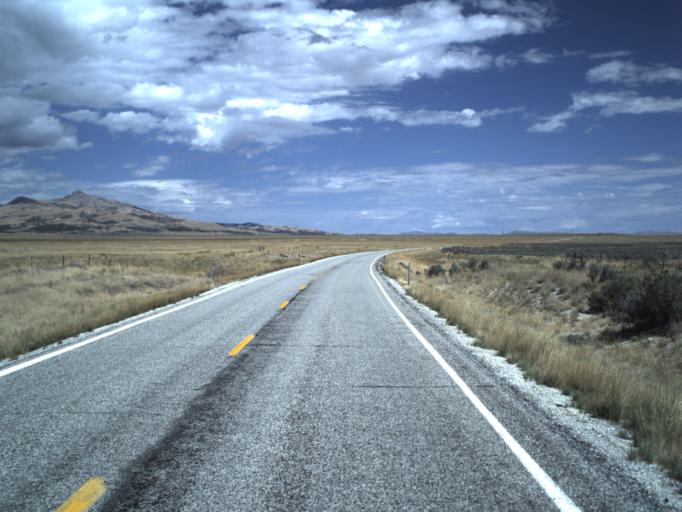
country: US
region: Idaho
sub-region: Oneida County
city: Malad City
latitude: 41.9464
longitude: -113.0809
